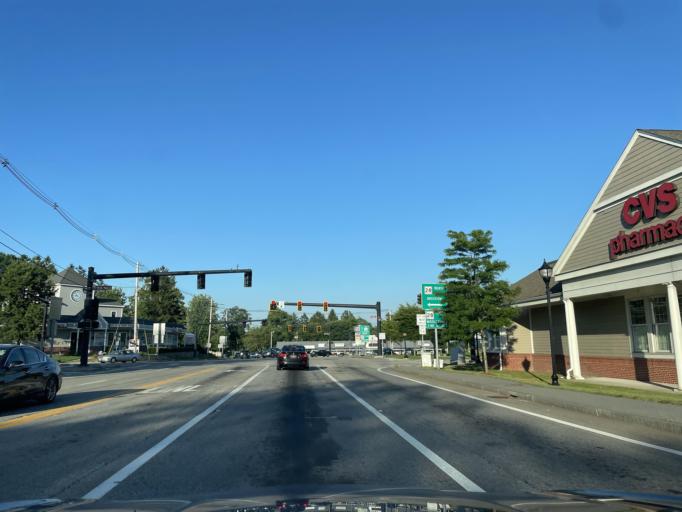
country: US
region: Massachusetts
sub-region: Plymouth County
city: West Bridgewater
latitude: 42.0188
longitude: -71.0088
